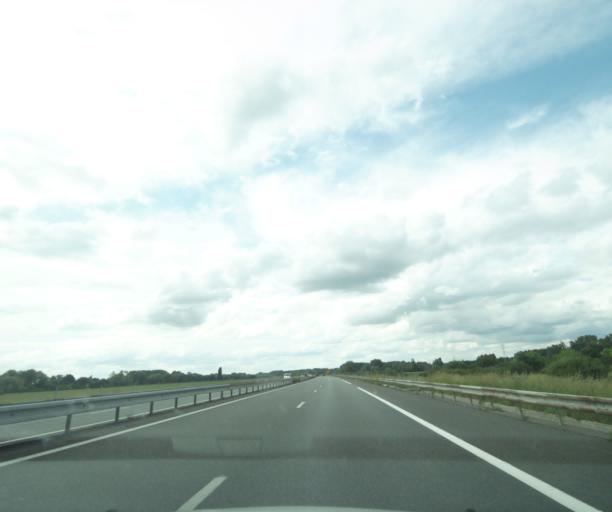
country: FR
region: Centre
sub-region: Departement du Cher
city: Vignoux-sur-Barangeon
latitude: 47.1907
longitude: 2.1622
